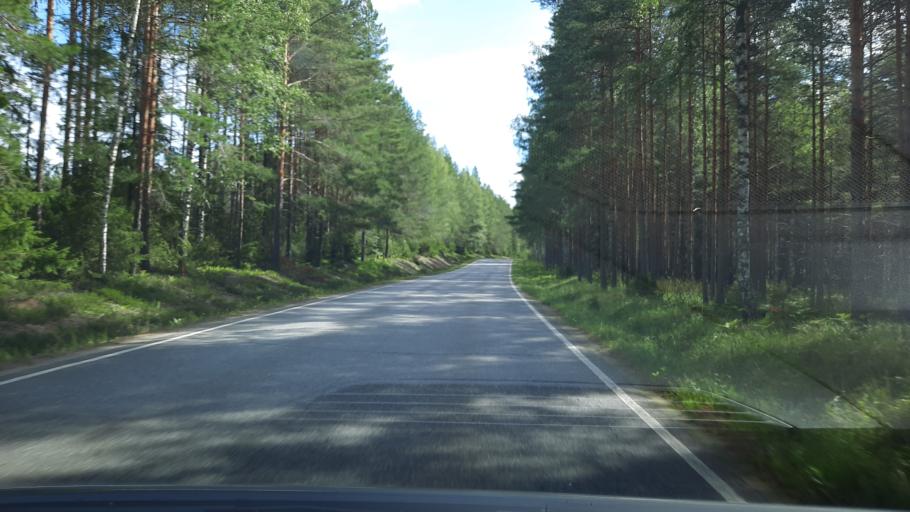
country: FI
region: Pirkanmaa
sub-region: Etelae-Pirkanmaa
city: Urjala
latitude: 61.1718
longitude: 23.3864
